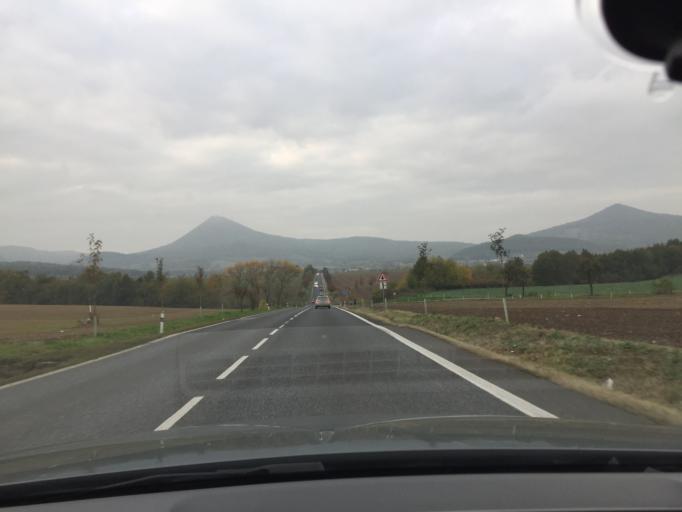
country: CZ
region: Ustecky
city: Velemin
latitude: 50.5280
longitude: 13.9942
